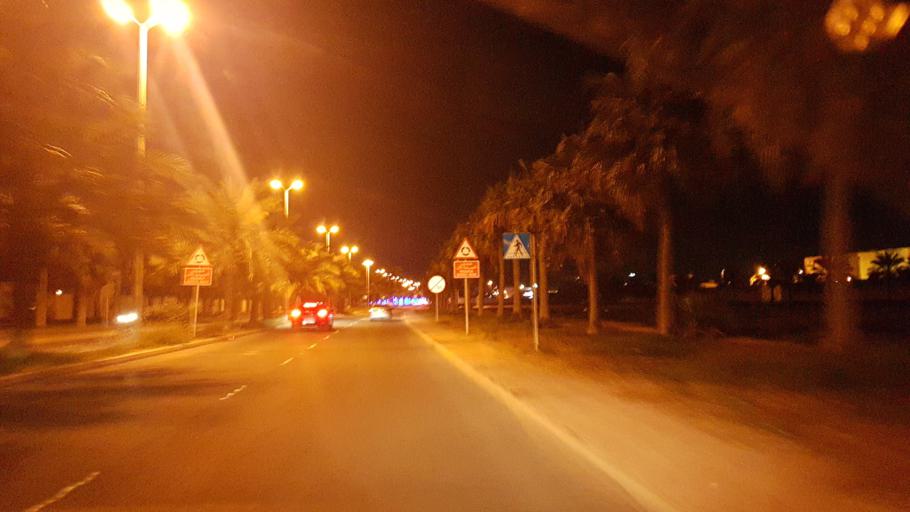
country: BH
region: Muharraq
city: Al Hadd
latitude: 26.2809
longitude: 50.6590
